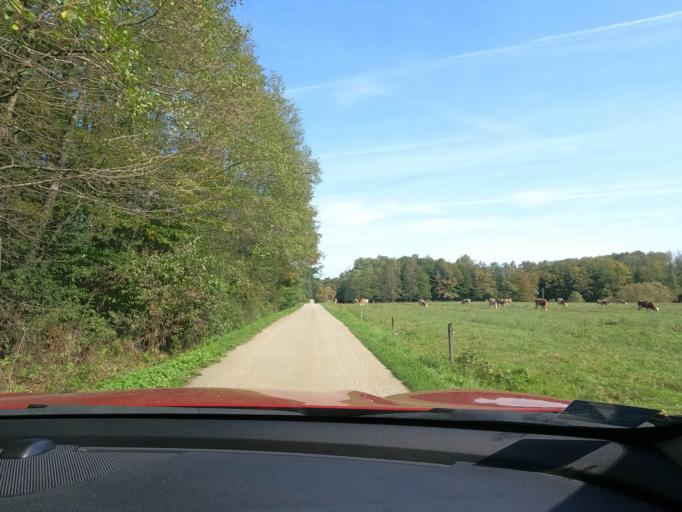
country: HR
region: Sisacko-Moslavacka
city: Petrinja
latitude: 45.3349
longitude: 16.2269
